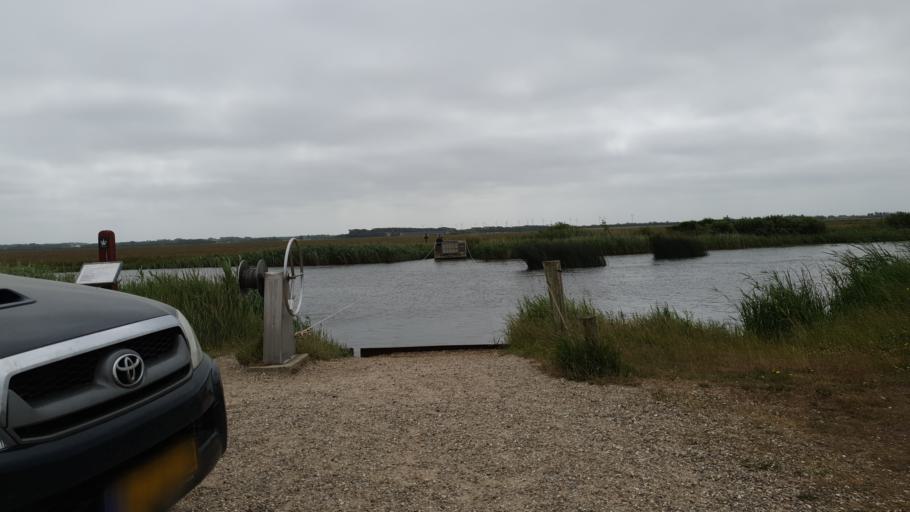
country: DK
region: Central Jutland
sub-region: Ringkobing-Skjern Kommune
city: Skjern
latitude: 55.9179
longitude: 8.4091
